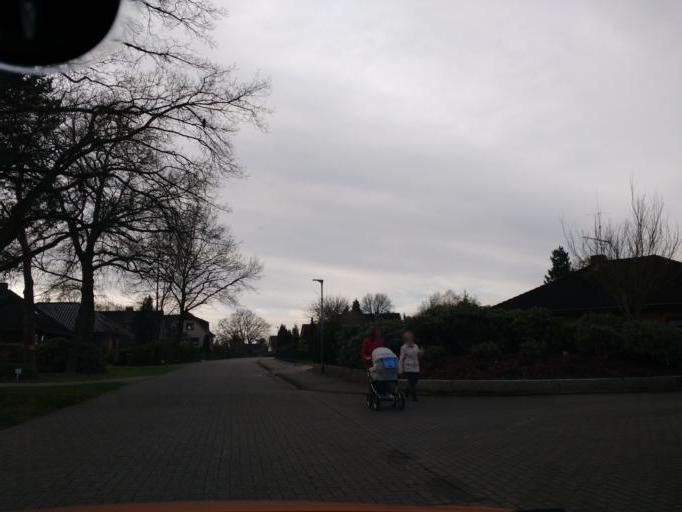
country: DE
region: Lower Saxony
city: Hude
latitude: 53.0995
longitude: 8.4643
